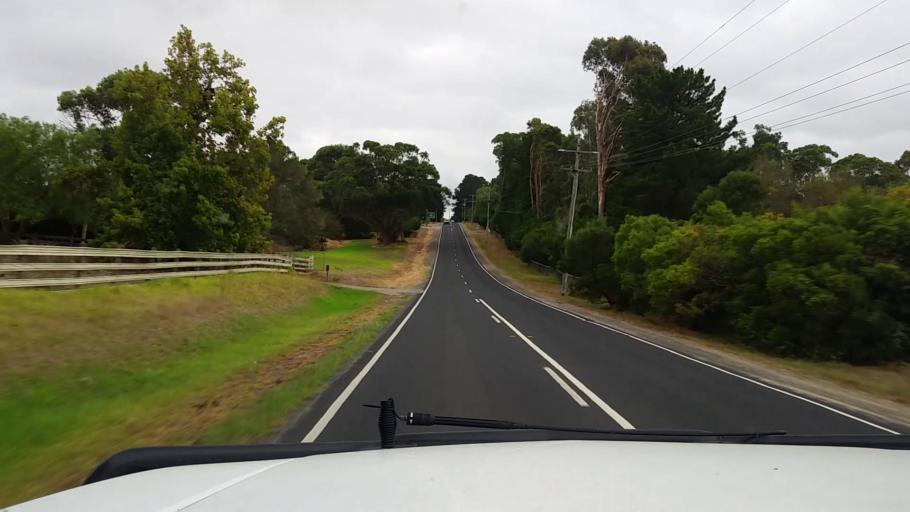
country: AU
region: Victoria
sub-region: Mornington Peninsula
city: Hastings
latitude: -38.2896
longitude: 145.1456
